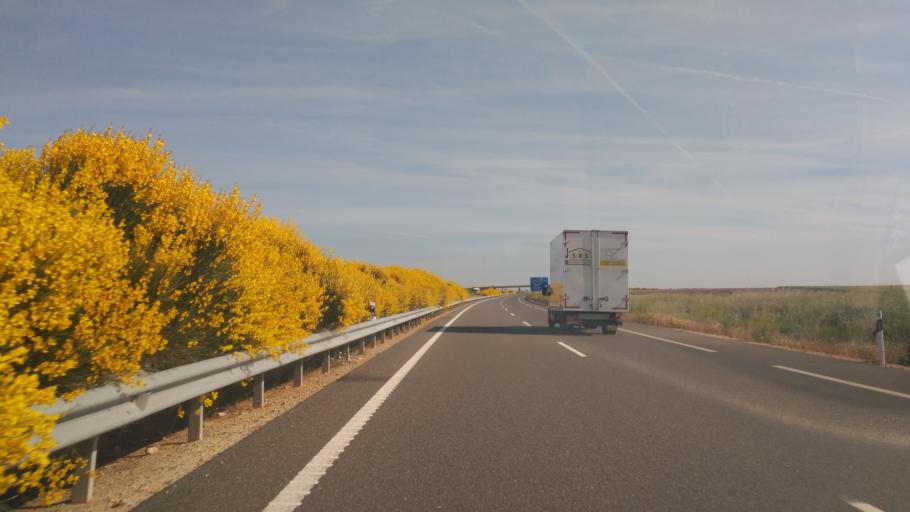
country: ES
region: Castille and Leon
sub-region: Provincia de Salamanca
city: Valdunciel
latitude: 41.0709
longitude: -5.6870
